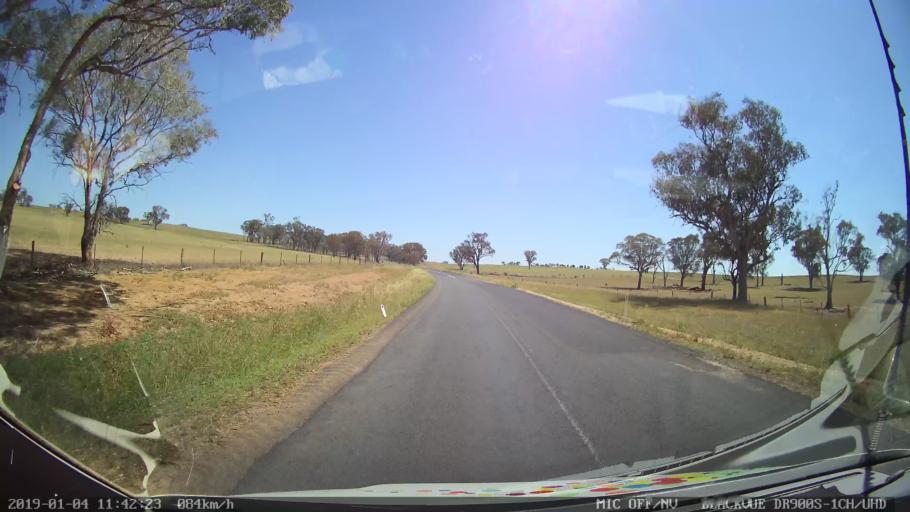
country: AU
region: New South Wales
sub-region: Cabonne
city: Molong
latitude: -32.9821
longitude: 148.7867
